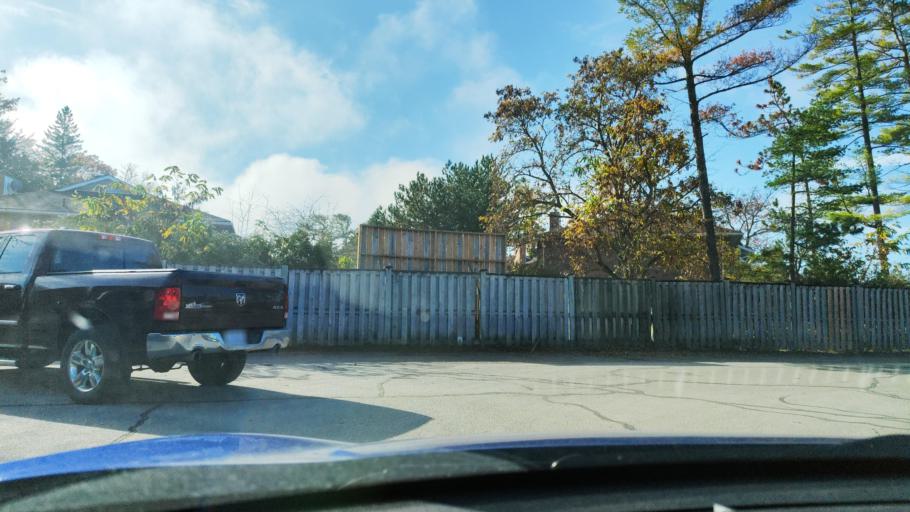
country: CA
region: Ontario
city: Wasaga Beach
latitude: 44.4886
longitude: -80.0507
